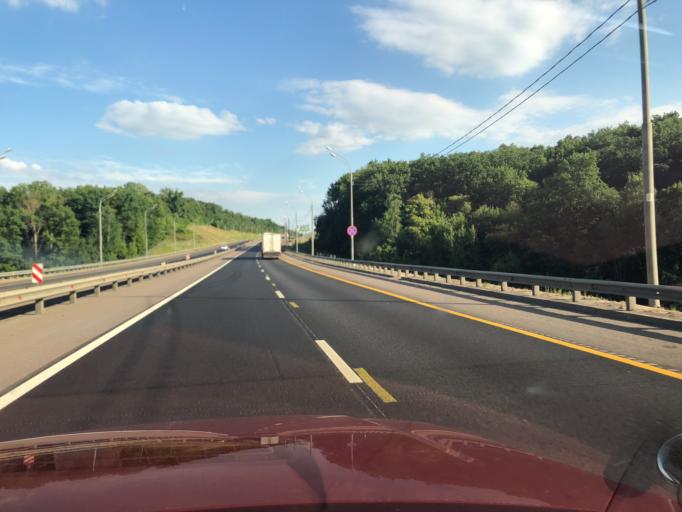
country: RU
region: Lipetsk
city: Zadonsk
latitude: 52.4051
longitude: 38.8555
